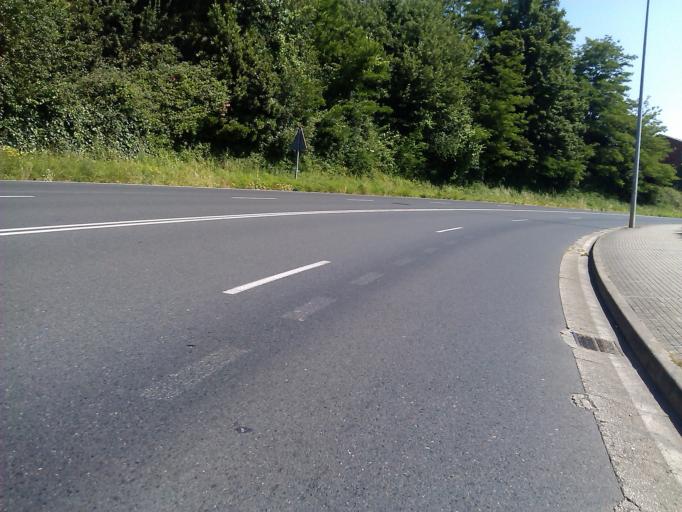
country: ES
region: Galicia
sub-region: Provincia da Coruna
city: Santiago de Compostela
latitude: 42.8691
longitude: -8.5442
